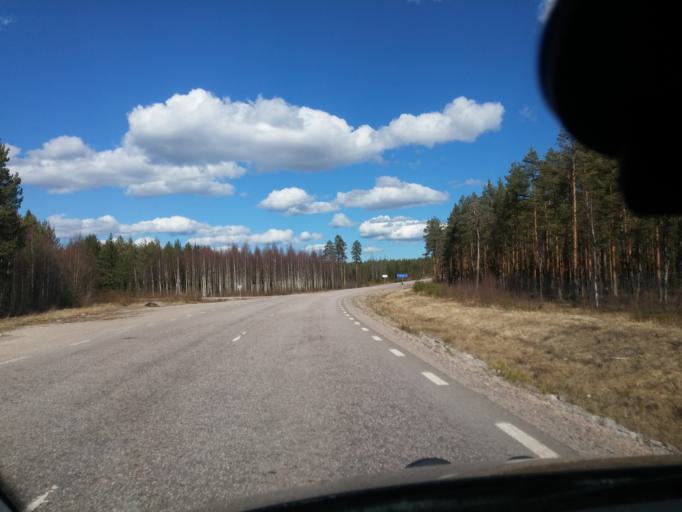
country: SE
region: Gaevleborg
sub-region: Ovanakers Kommun
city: Edsbyn
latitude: 61.2856
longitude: 15.9059
